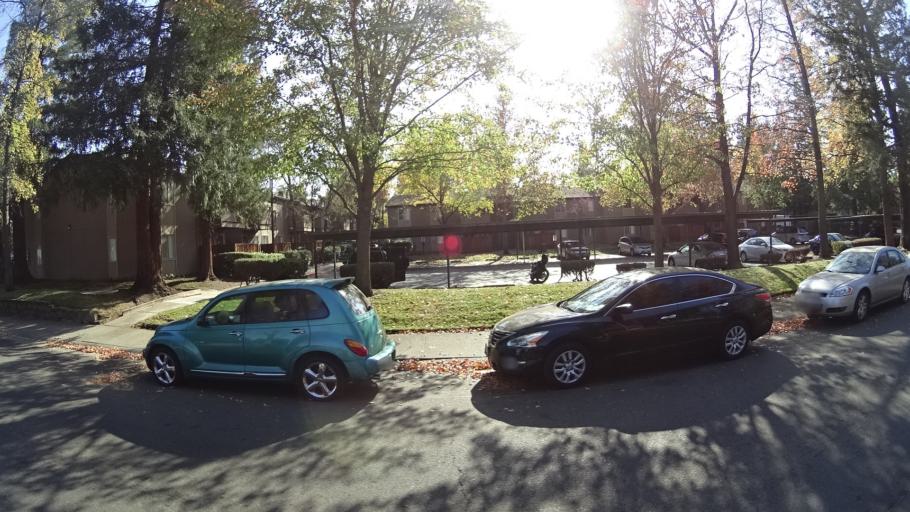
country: US
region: California
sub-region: Sacramento County
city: Citrus Heights
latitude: 38.6806
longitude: -121.2813
